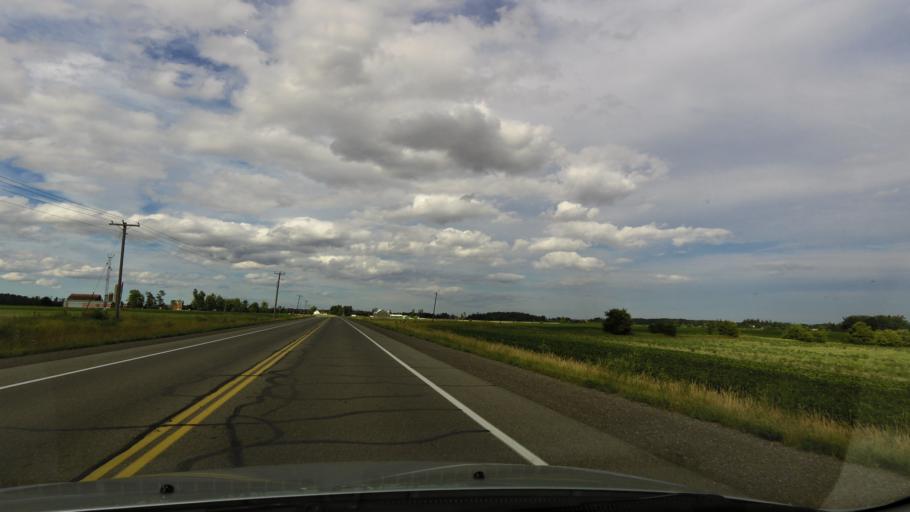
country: CA
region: Ontario
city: Brampton
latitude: 43.6792
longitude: -79.8840
